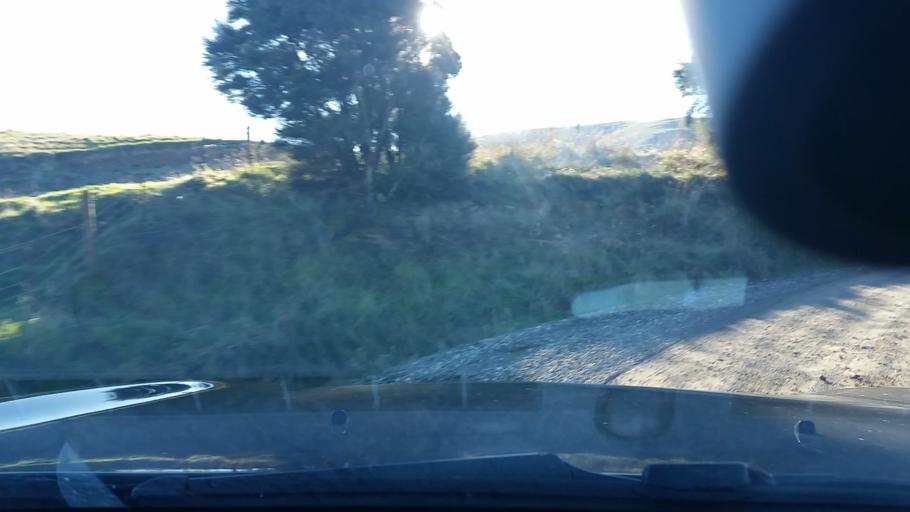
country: NZ
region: Marlborough
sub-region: Marlborough District
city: Blenheim
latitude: -41.5871
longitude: 174.0866
